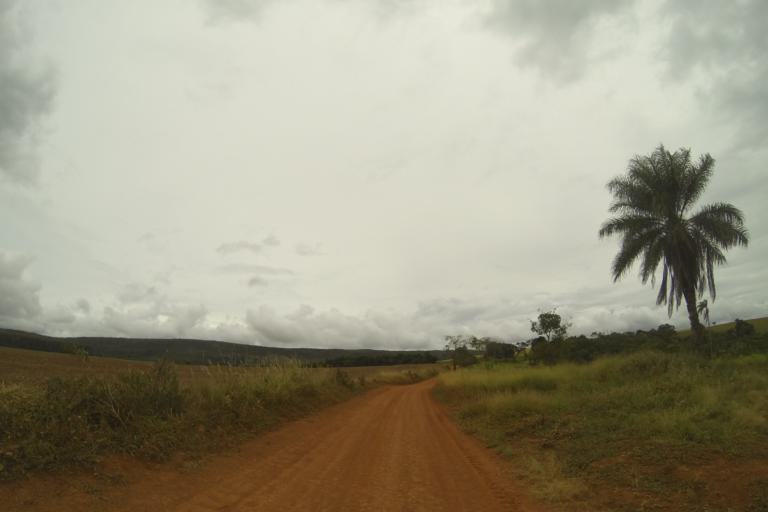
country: BR
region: Minas Gerais
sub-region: Ibia
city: Ibia
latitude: -19.7439
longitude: -46.6160
